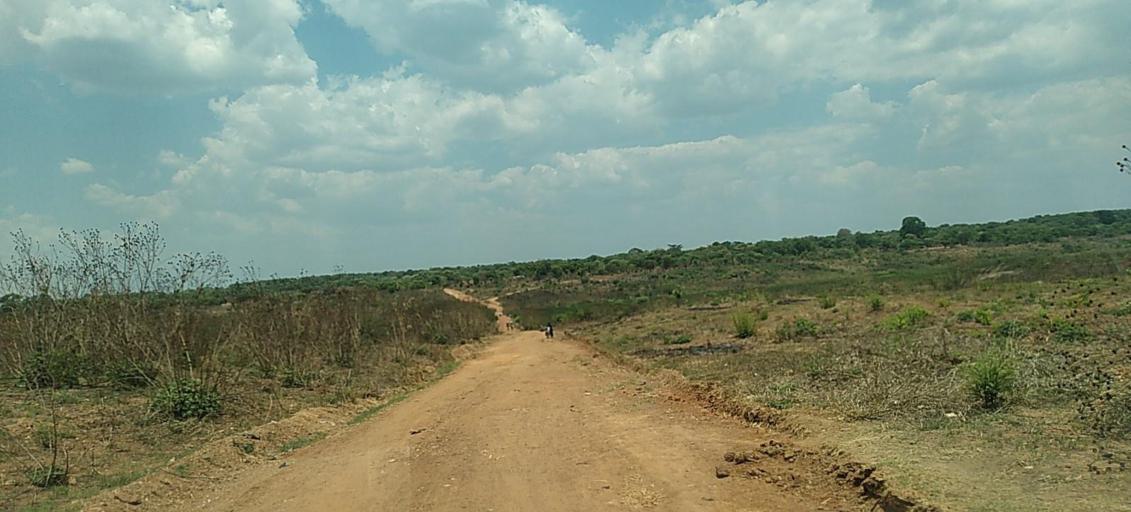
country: ZM
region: Copperbelt
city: Luanshya
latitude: -13.3707
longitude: 28.4159
